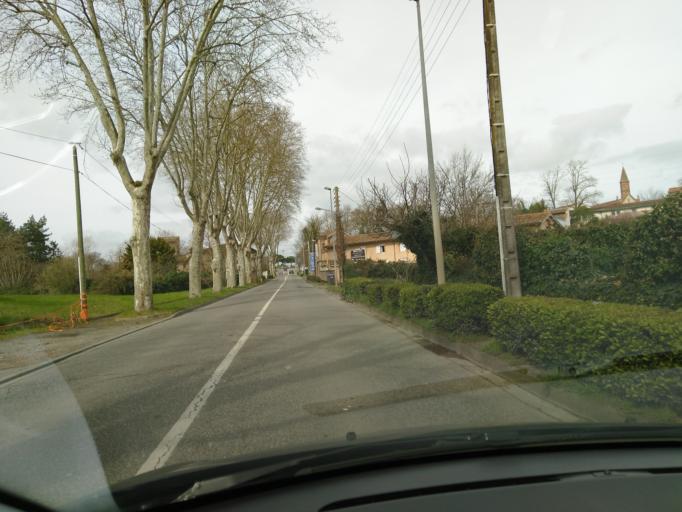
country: FR
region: Midi-Pyrenees
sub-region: Departement de la Haute-Garonne
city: Seilh
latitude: 43.6934
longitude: 1.3537
